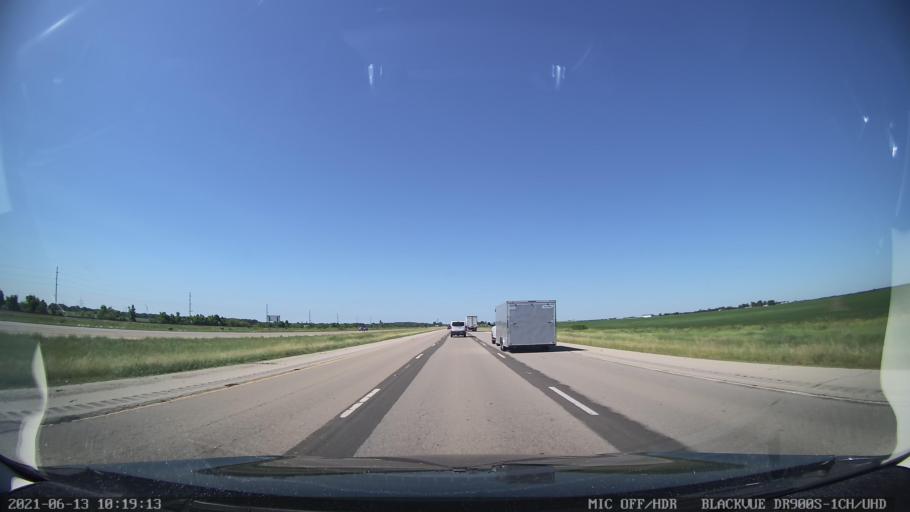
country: US
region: Illinois
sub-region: Logan County
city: Lincoln
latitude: 40.0861
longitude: -89.4295
